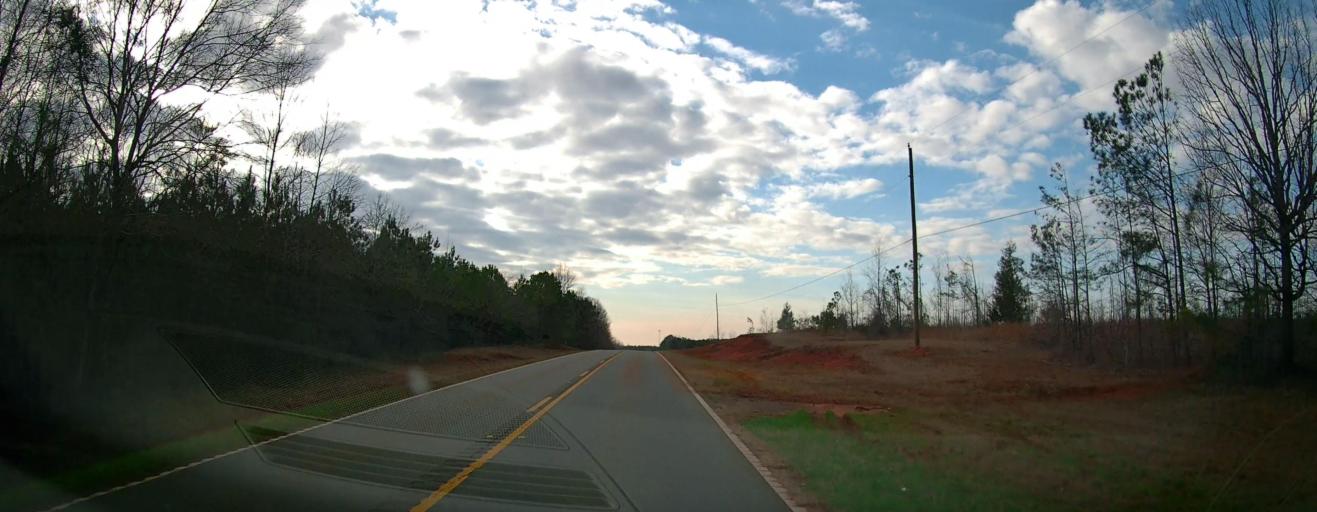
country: US
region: Georgia
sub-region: Harris County
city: Hamilton
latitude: 32.6860
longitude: -84.7707
